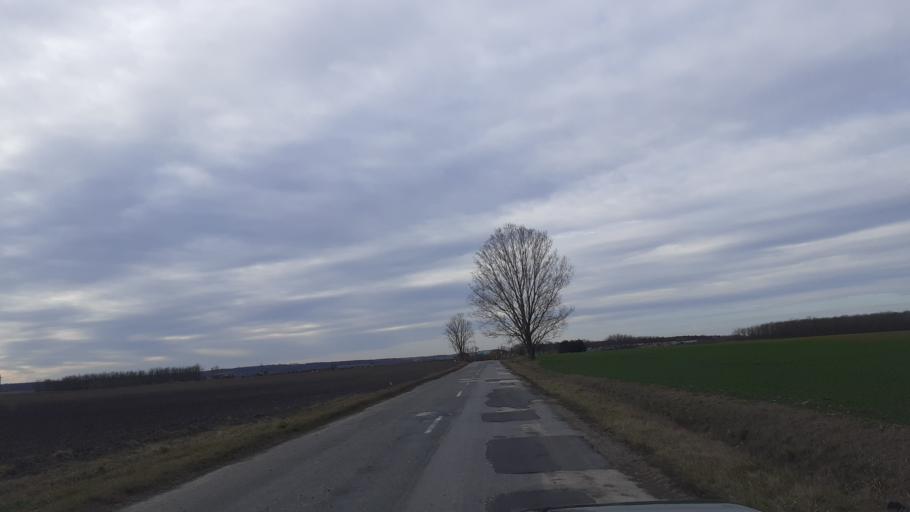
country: HU
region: Fejer
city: Sarbogard
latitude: 46.9078
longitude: 18.5738
